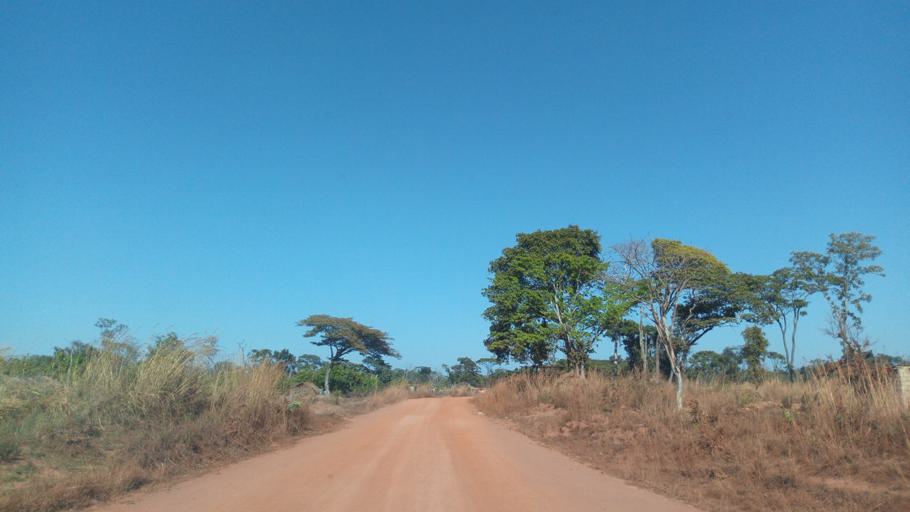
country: ZM
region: Luapula
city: Mwense
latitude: -10.7035
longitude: 28.3766
